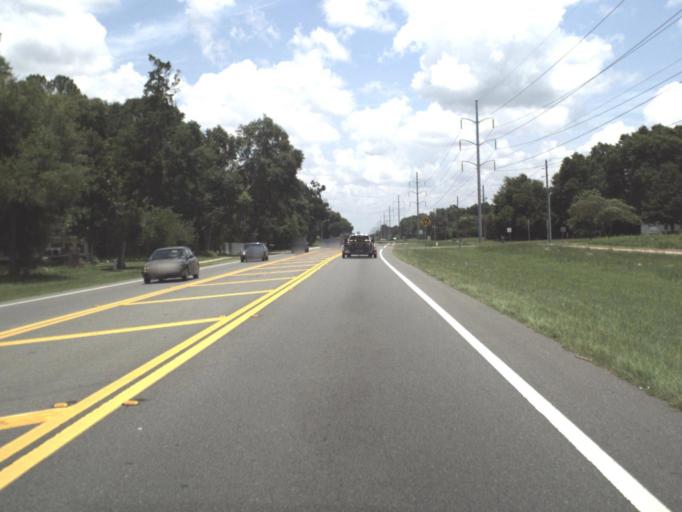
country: US
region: Florida
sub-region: Alachua County
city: Archer
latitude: 29.5953
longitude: -82.4281
